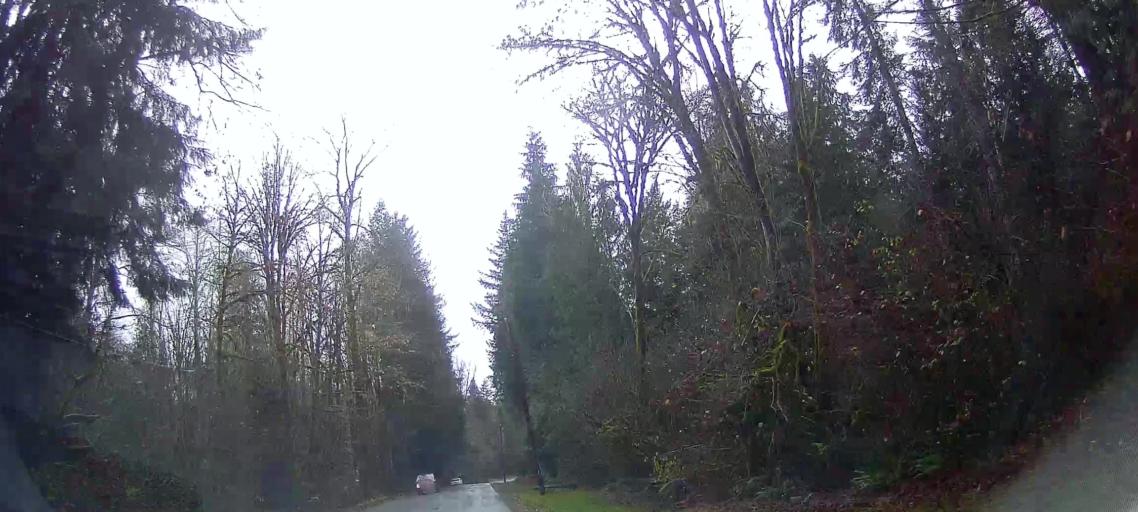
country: US
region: Washington
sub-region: Snohomish County
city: Darrington
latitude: 48.5290
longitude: -121.4115
